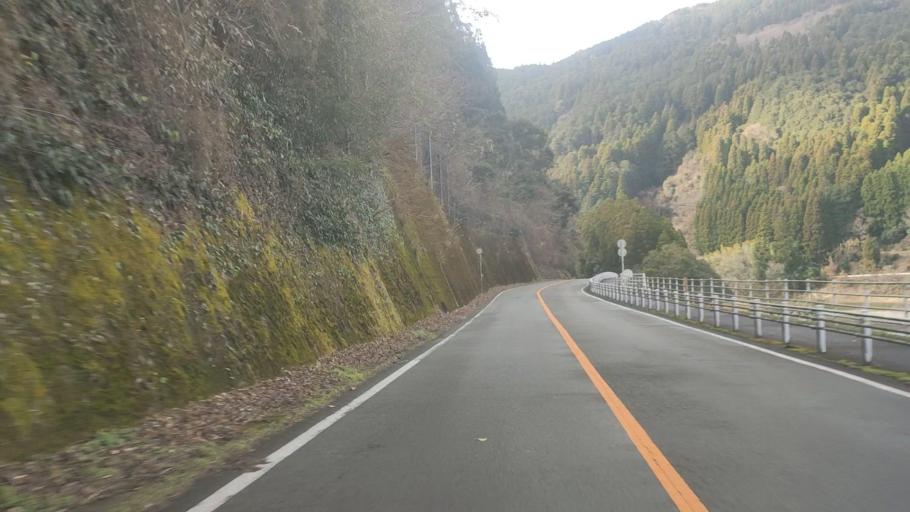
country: JP
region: Kumamoto
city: Hitoyoshi
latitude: 32.2933
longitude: 130.8447
